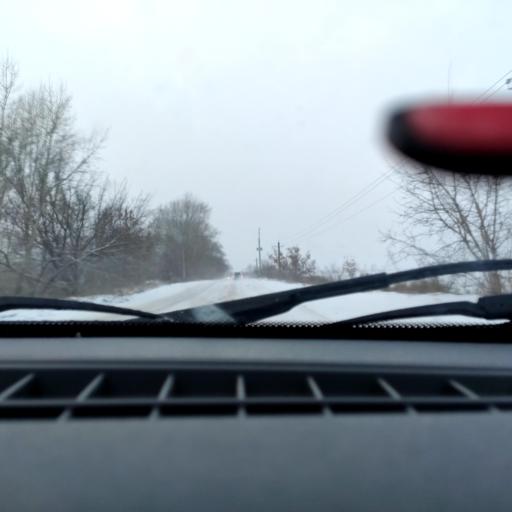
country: RU
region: Bashkortostan
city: Blagoveshchensk
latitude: 54.9126
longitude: 55.9943
